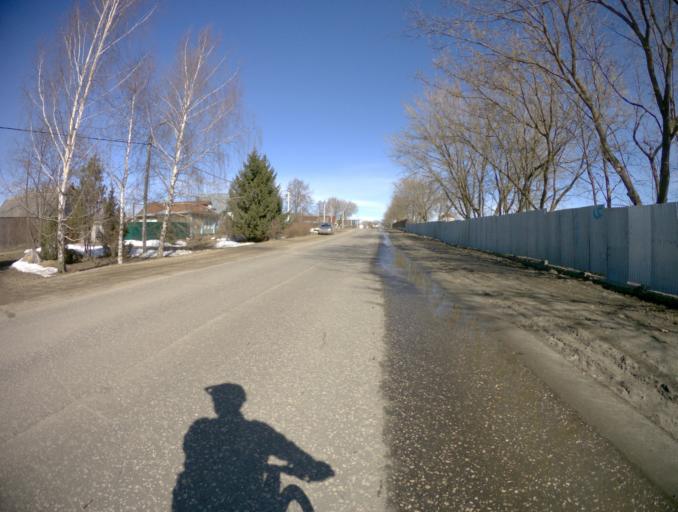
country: RU
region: Vladimir
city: Suzdal'
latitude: 56.4326
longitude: 40.4237
